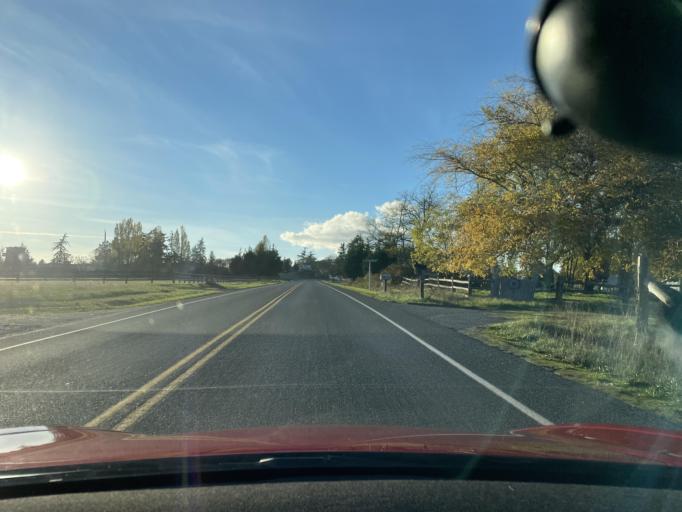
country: US
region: Washington
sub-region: San Juan County
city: Friday Harbor
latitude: 48.5108
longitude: -123.0306
